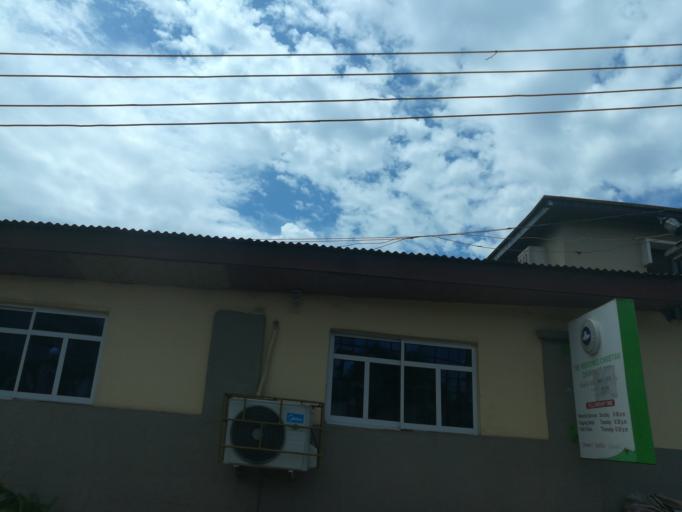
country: NG
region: Lagos
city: Agege
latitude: 6.6064
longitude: 3.3253
